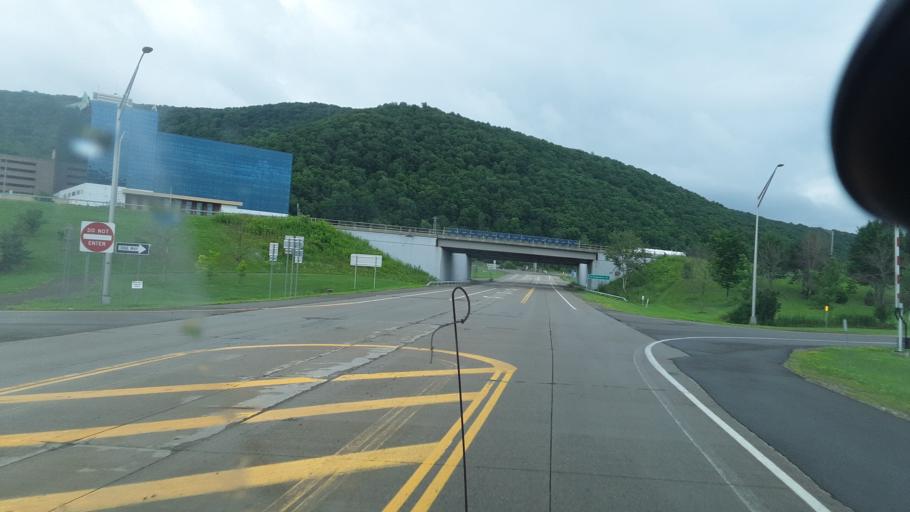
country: US
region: New York
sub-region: Cattaraugus County
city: Salamanca
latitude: 42.1553
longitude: -78.7509
